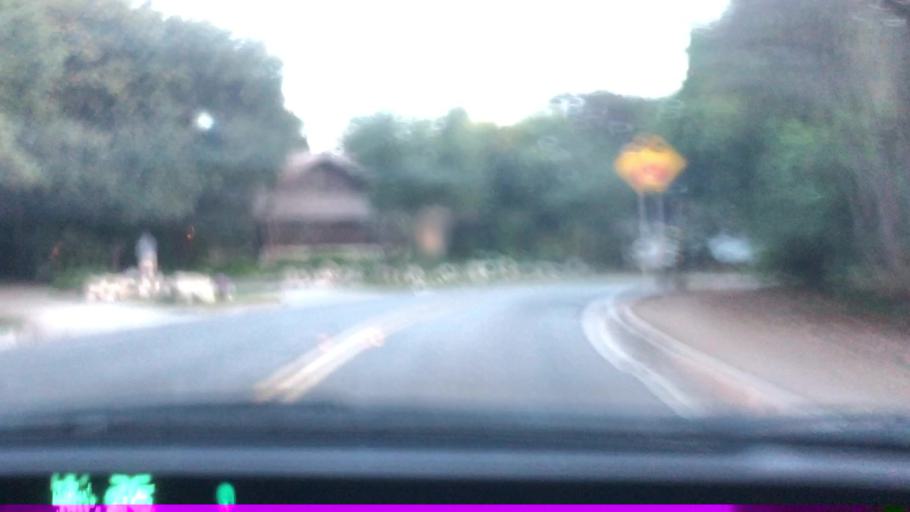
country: US
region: California
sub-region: Los Angeles County
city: Pasadena
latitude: 34.1370
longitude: -118.1662
